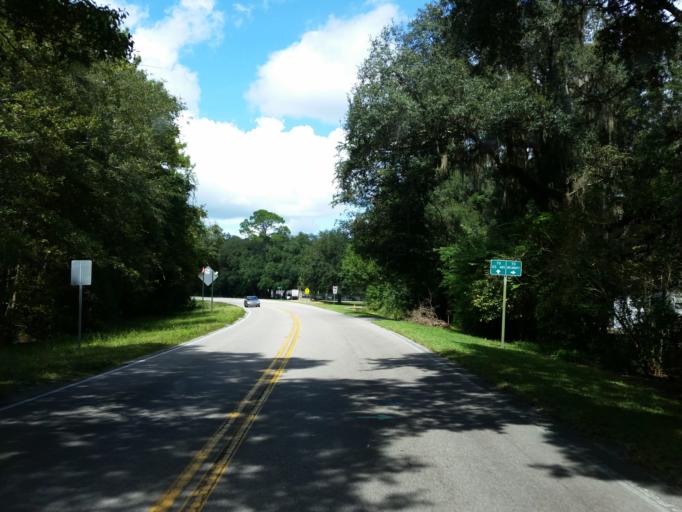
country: US
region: Florida
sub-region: Alachua County
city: Gainesville
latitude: 29.5027
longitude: -82.2903
